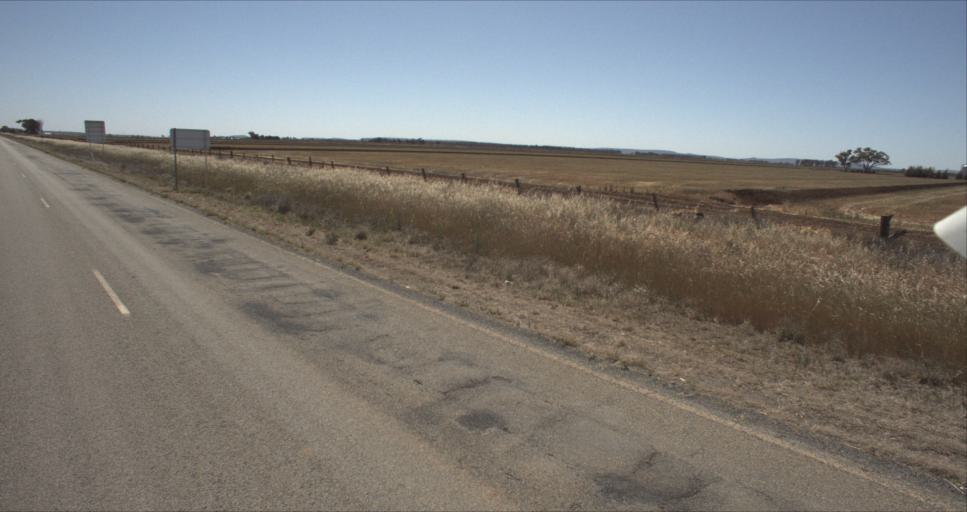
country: AU
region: New South Wales
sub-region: Leeton
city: Leeton
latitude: -34.5177
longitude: 146.2839
